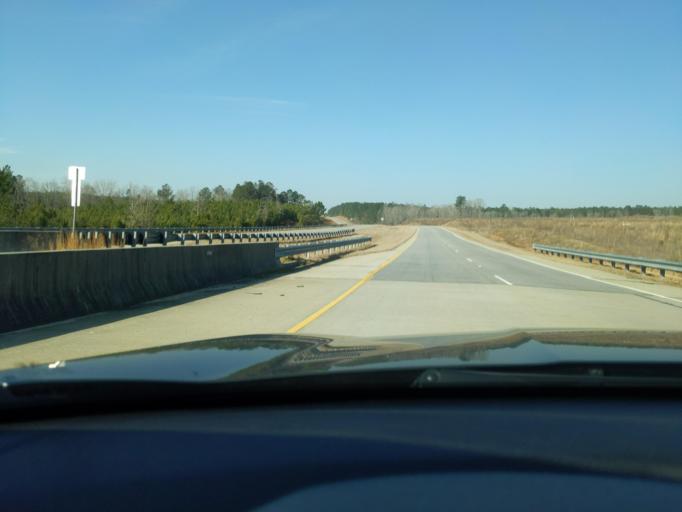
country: US
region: South Carolina
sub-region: Abbeville County
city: Abbeville
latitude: 34.1133
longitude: -82.4778
